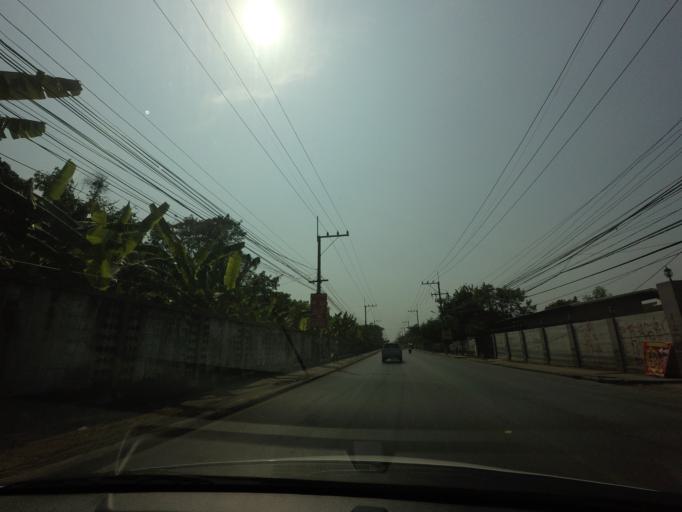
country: TH
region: Nakhon Pathom
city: Sam Phran
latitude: 13.7148
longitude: 100.2609
